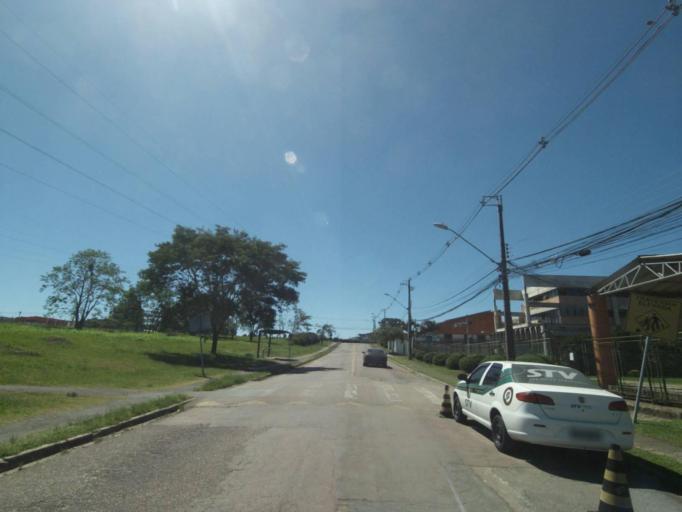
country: BR
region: Parana
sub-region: Curitiba
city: Curitiba
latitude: -25.4699
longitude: -49.3470
